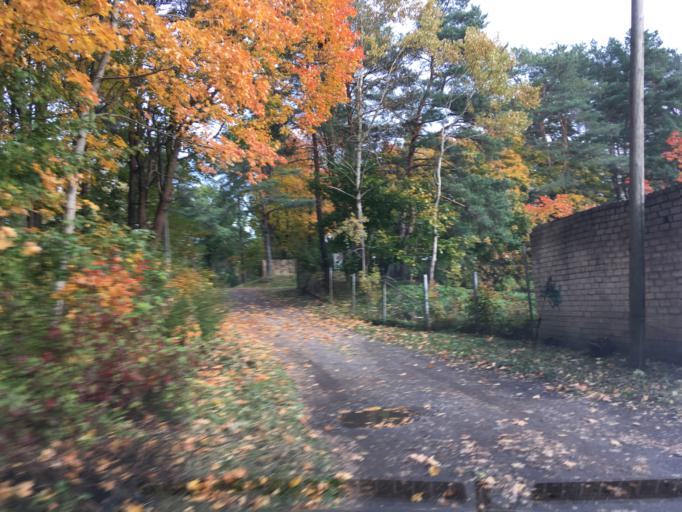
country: EE
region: Harju
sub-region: Saue vald
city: Laagri
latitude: 59.3738
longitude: 24.6474
